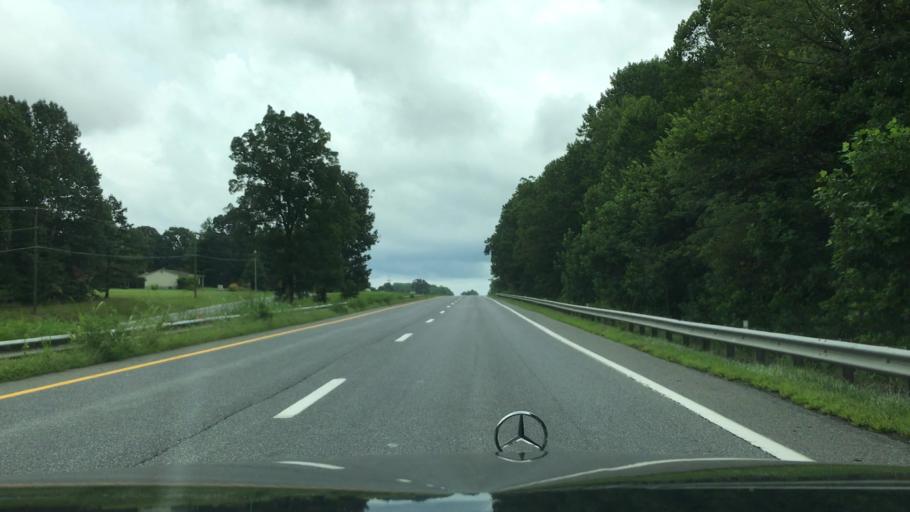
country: US
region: Virginia
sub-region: Appomattox County
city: Appomattox
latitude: 37.2804
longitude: -78.7025
